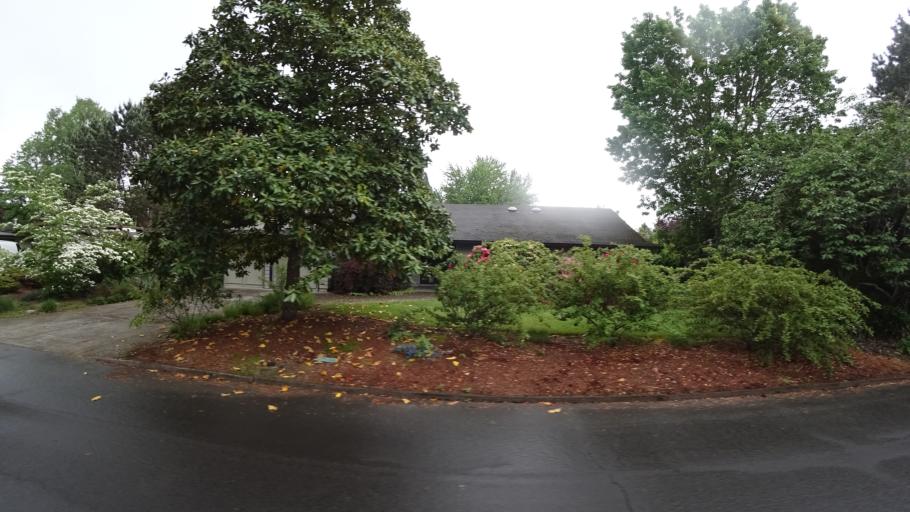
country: US
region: Oregon
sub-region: Washington County
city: Garden Home-Whitford
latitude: 45.4700
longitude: -122.7685
